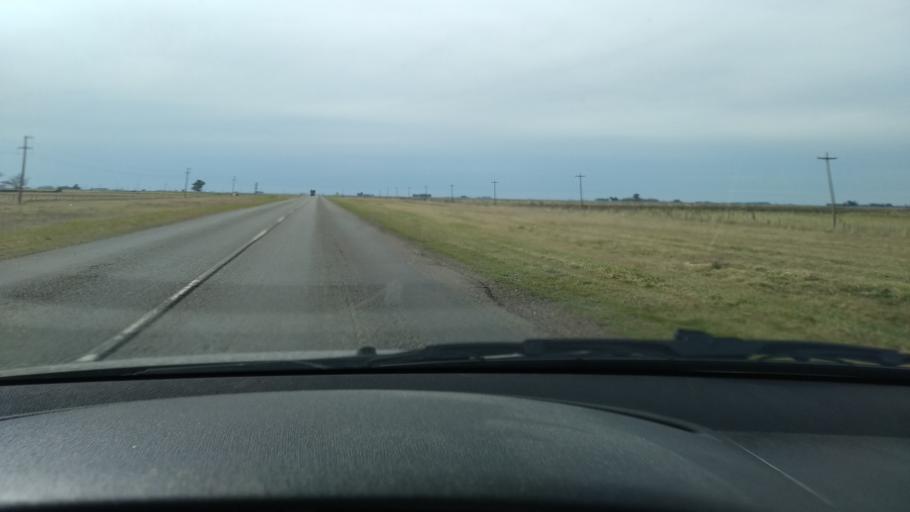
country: AR
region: Buenos Aires
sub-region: Partido de Azul
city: Azul
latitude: -36.6821
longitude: -59.7283
